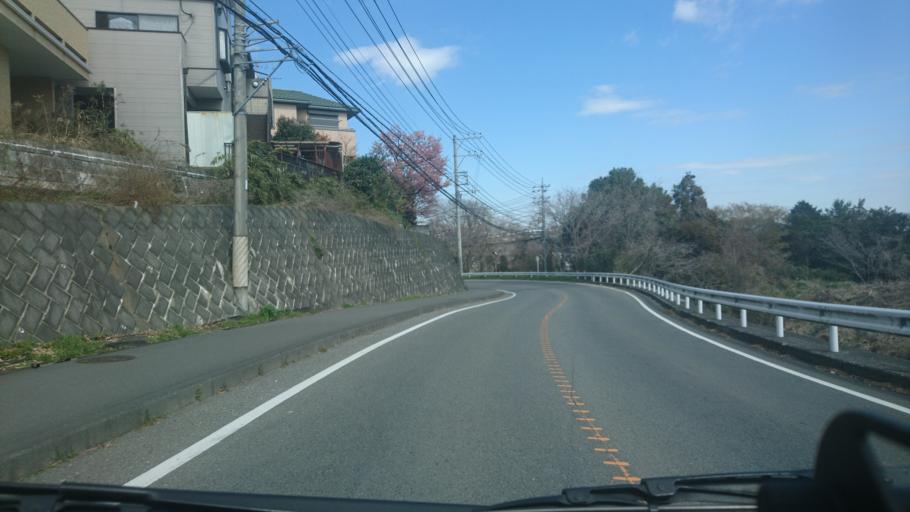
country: JP
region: Kanagawa
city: Zama
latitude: 35.5332
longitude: 139.3315
